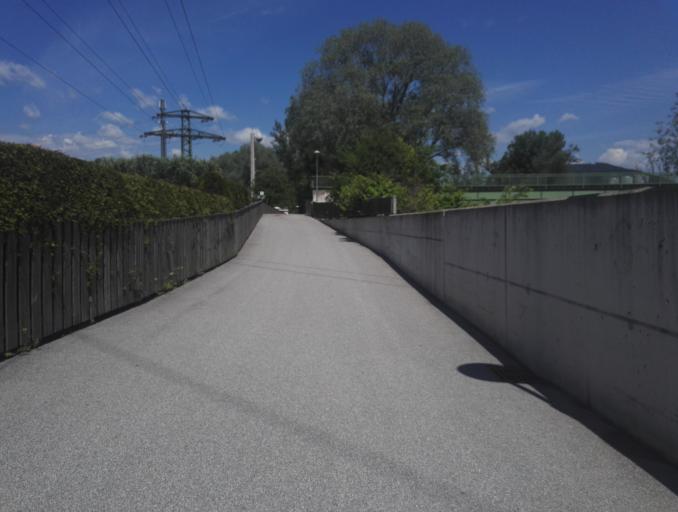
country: AT
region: Styria
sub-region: Politischer Bezirk Graz-Umgebung
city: Gratkorn
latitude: 47.1231
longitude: 15.3465
